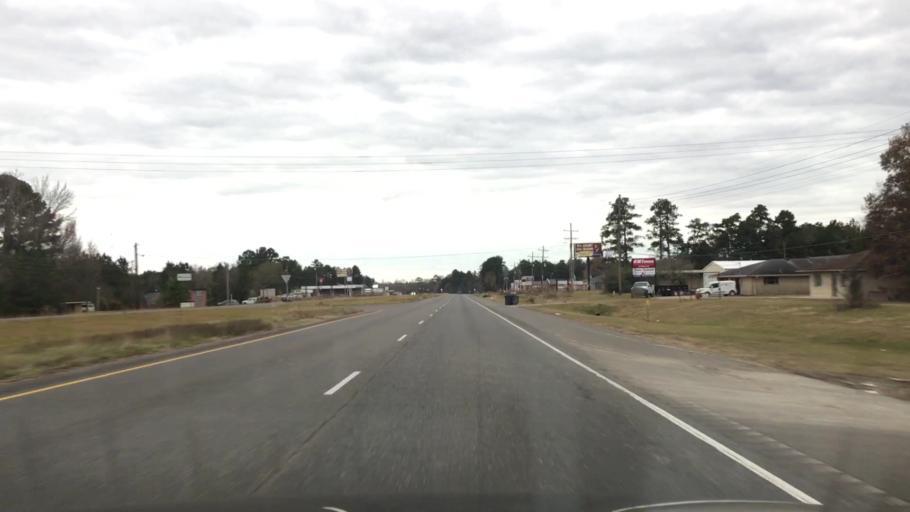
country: US
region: Louisiana
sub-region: Vernon Parish
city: New Llano
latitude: 31.0772
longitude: -93.2731
